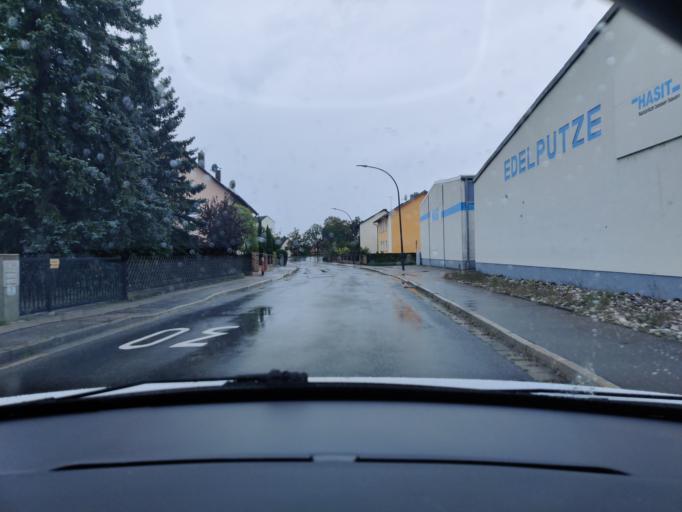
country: DE
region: Bavaria
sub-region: Upper Palatinate
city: Schwarzenfeld
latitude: 49.3896
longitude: 12.1287
